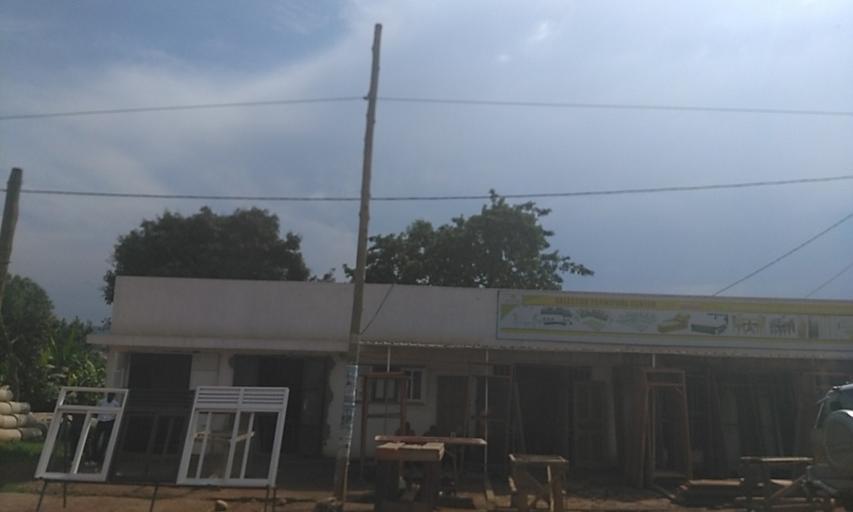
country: UG
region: Central Region
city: Kampala Central Division
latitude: 0.3033
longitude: 32.5239
